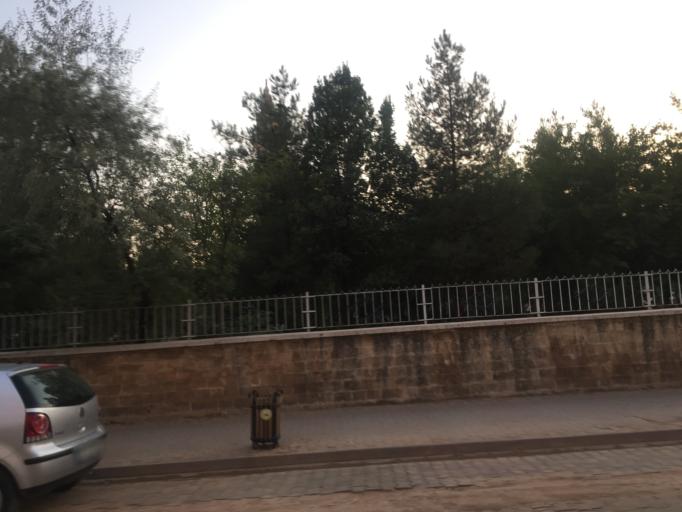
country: TR
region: Mardin
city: Midyat
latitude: 37.4282
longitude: 41.3390
